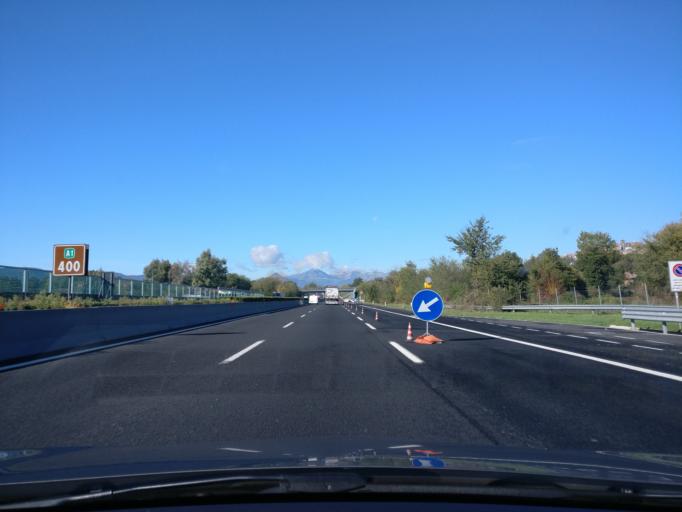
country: IT
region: Latium
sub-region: Provincia di Frosinone
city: Pofi
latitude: 41.5549
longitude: 13.4306
